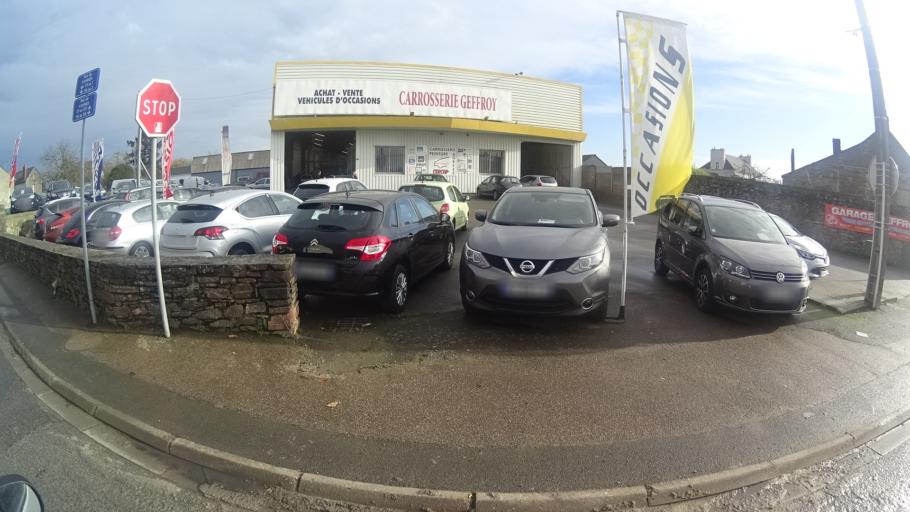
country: FR
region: Brittany
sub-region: Departement d'Ille-et-Vilaine
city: Redon
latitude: 47.6433
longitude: -2.0925
